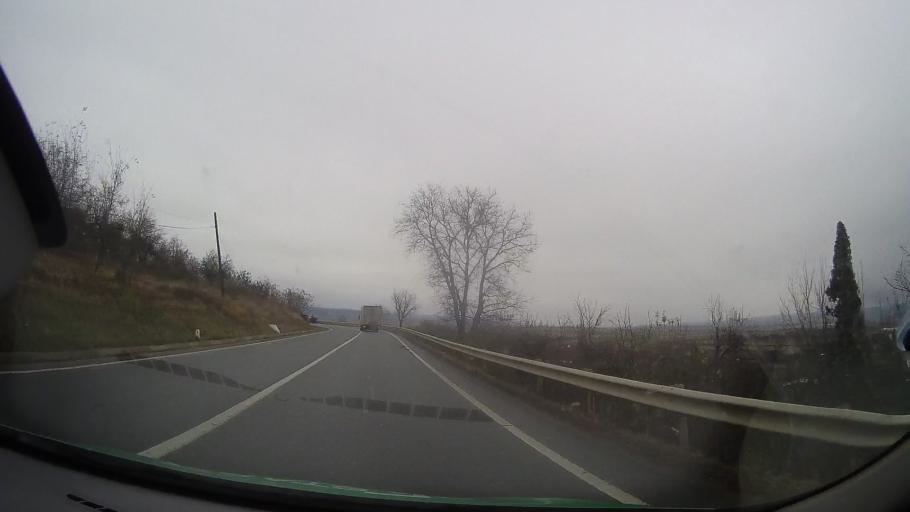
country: RO
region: Mures
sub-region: Comuna Breaza
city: Breaza
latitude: 46.7631
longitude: 24.6594
